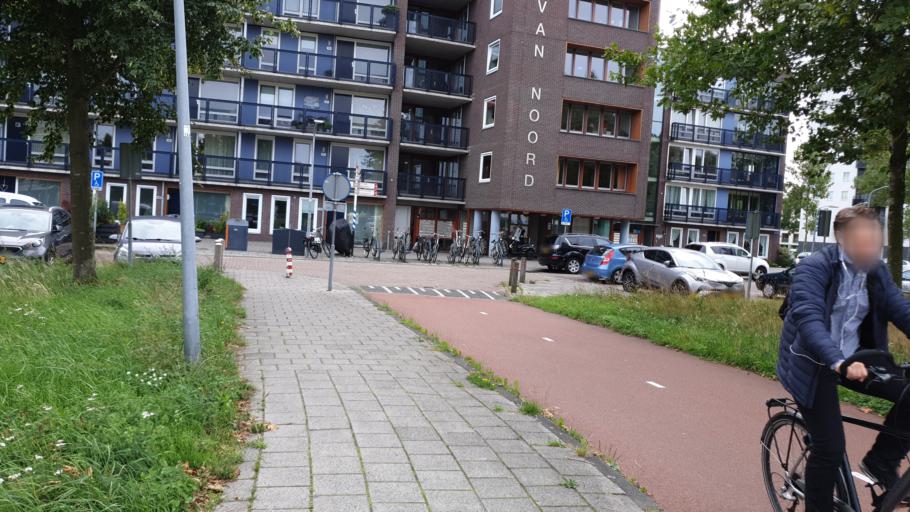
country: NL
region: North Holland
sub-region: Gemeente Bloemendaal
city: Bloemendaal
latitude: 52.4223
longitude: 4.6486
